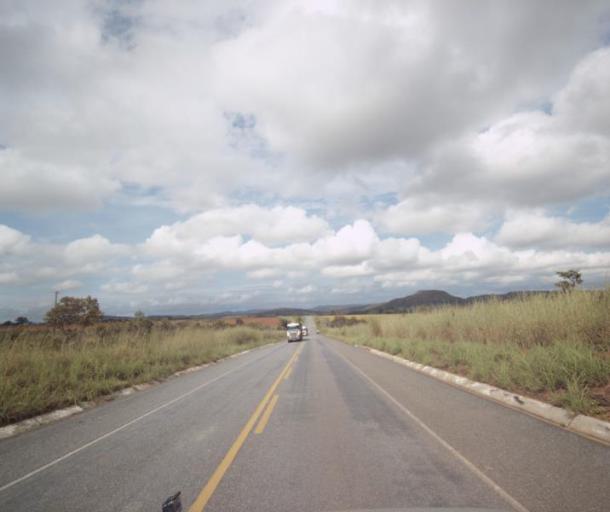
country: BR
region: Goias
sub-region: Pirenopolis
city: Pirenopolis
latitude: -15.5872
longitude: -48.6340
